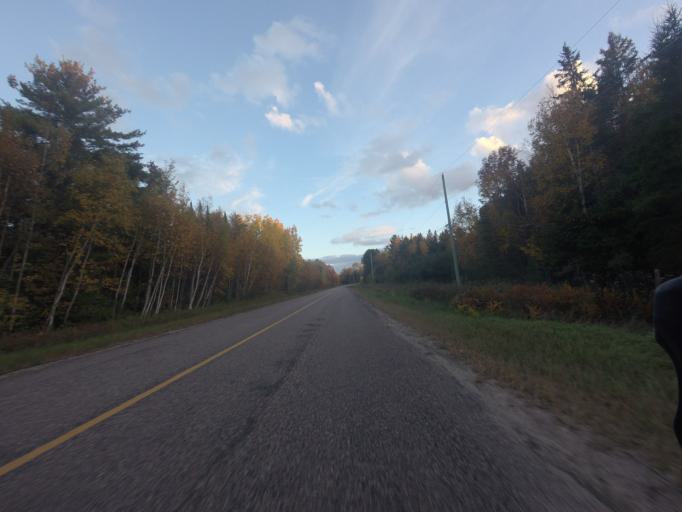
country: CA
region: Ontario
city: Renfrew
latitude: 45.4202
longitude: -76.9530
